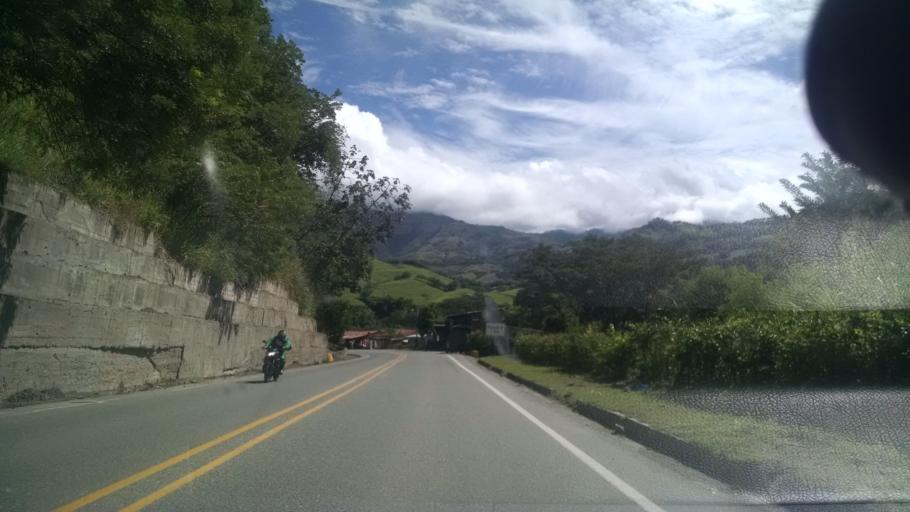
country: CO
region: Caldas
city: Supia
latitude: 5.3834
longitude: -75.6047
